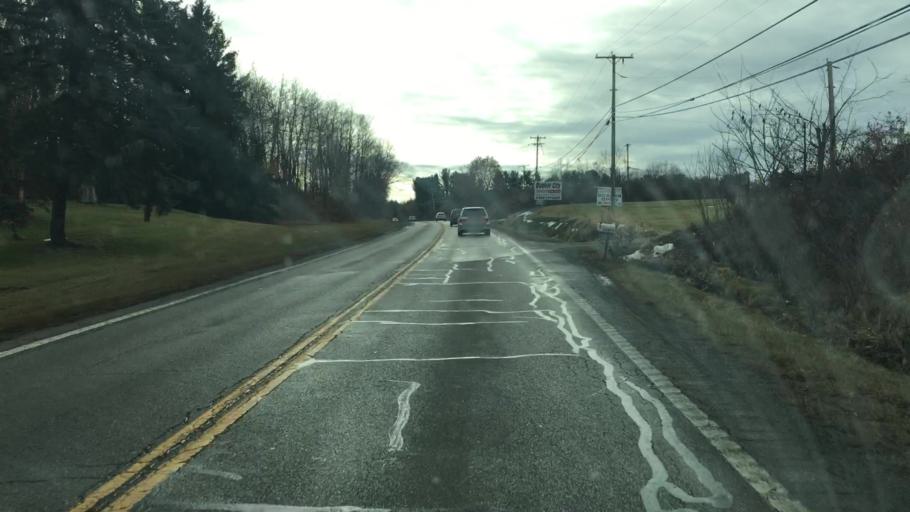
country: US
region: Ohio
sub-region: Columbiana County
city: Salem
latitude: 40.9374
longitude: -80.8401
